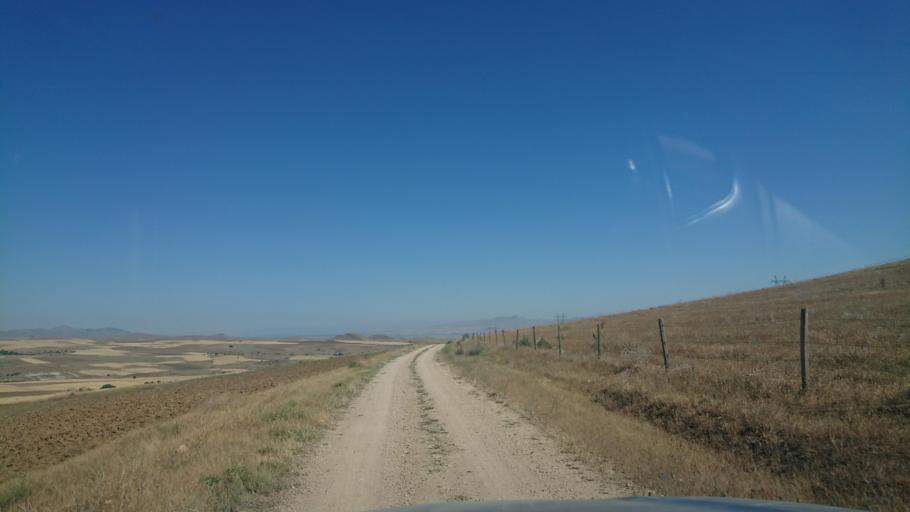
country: TR
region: Aksaray
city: Agacoren
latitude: 38.9161
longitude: 33.8933
